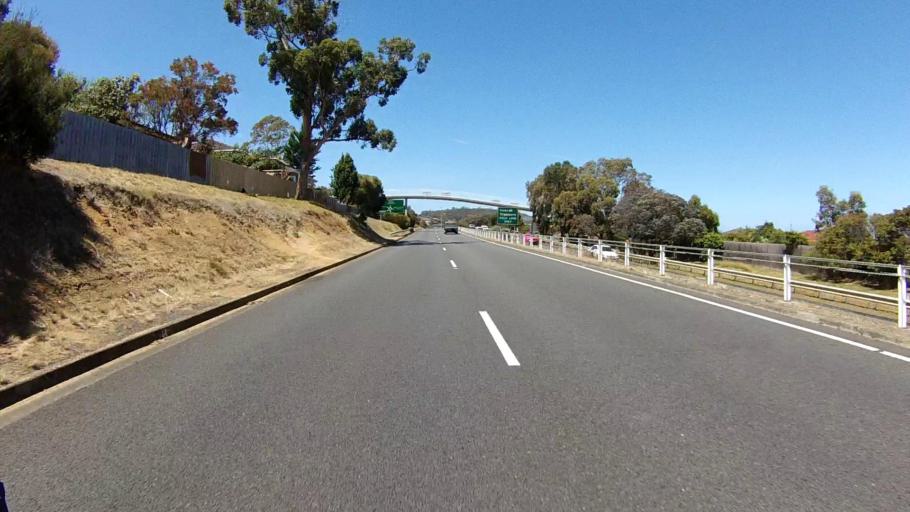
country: AU
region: Tasmania
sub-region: Clarence
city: Howrah
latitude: -42.8751
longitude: 147.4034
